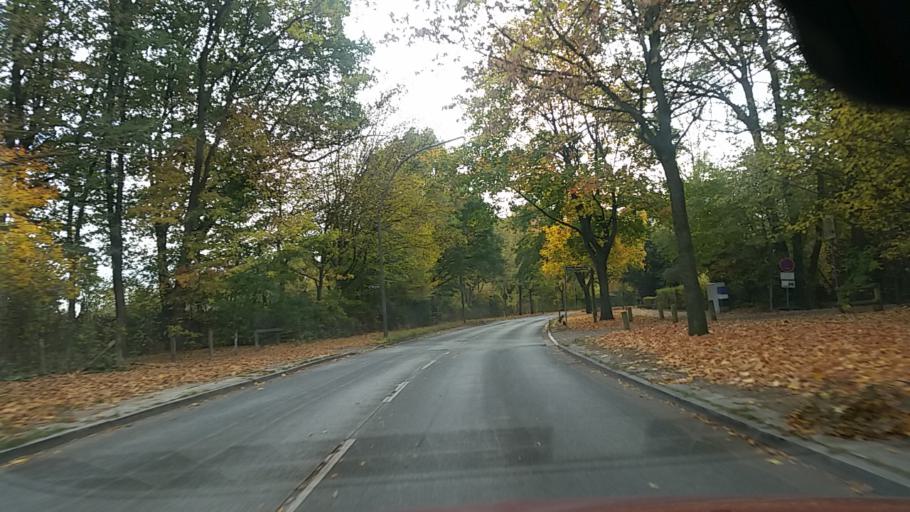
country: DE
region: Hamburg
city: Hummelsbuettel
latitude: 53.6523
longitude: 10.0232
